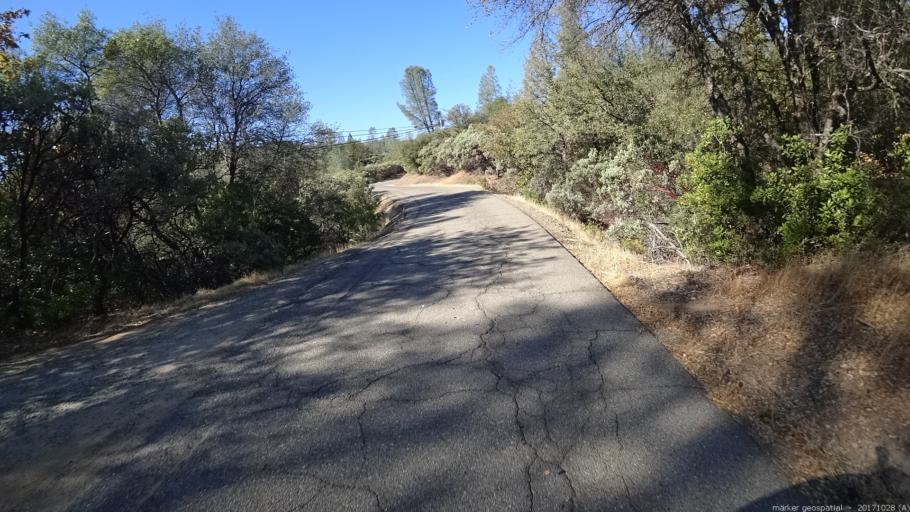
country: US
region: California
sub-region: Shasta County
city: Shasta
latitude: 40.5974
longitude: -122.4633
